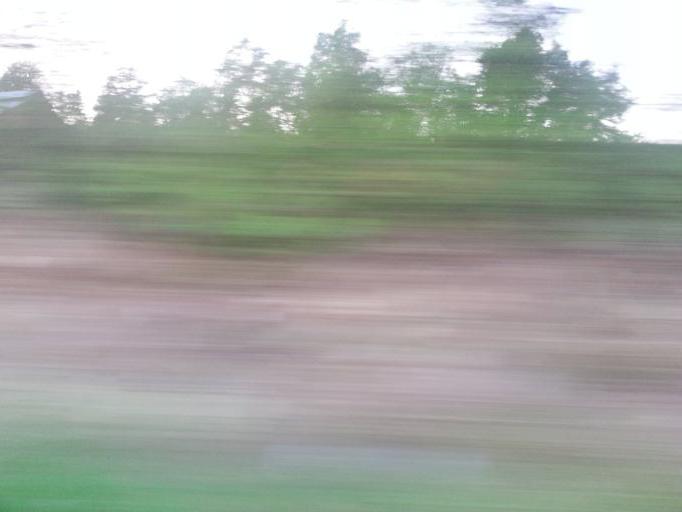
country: US
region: Tennessee
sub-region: Union County
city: Condon
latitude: 36.1658
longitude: -83.8151
